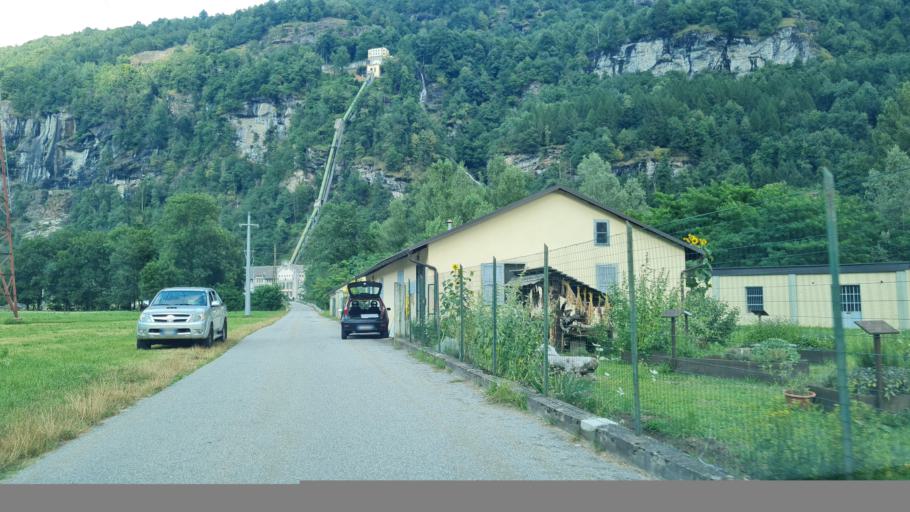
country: IT
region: Piedmont
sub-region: Provincia Verbano-Cusio-Ossola
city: Baceno
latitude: 46.2453
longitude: 8.3277
